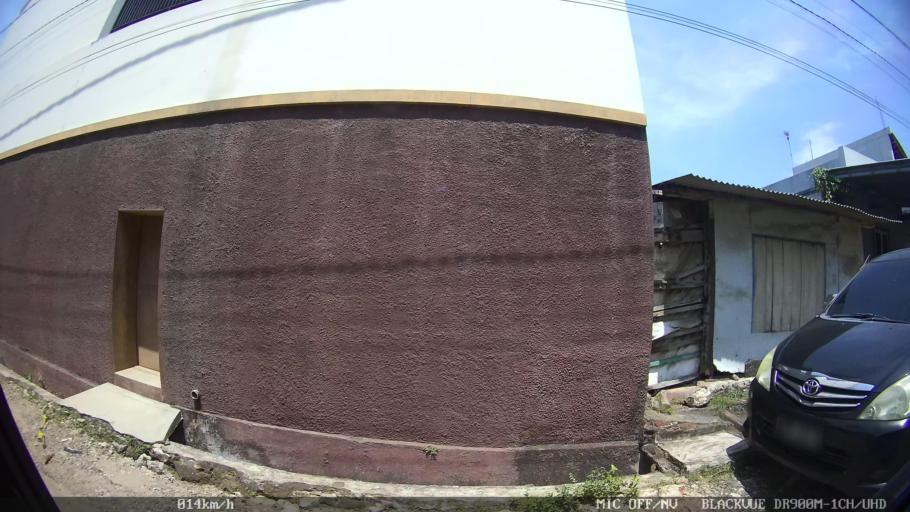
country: ID
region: Lampung
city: Kedaton
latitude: -5.3897
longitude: 105.2714
